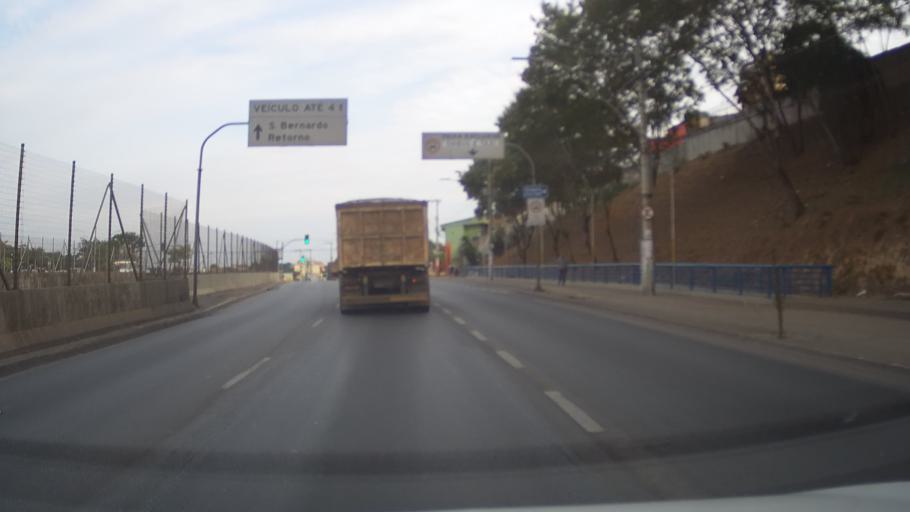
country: BR
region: Minas Gerais
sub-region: Belo Horizonte
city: Belo Horizonte
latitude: -19.8480
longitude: -43.9326
